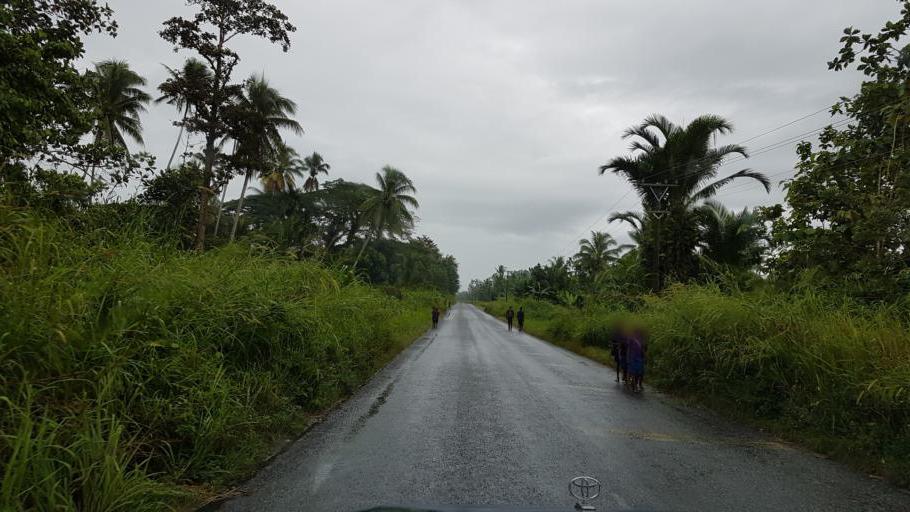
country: PG
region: Northern Province
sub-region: Sohe
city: Popondetta
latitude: -8.8172
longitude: 148.2414
